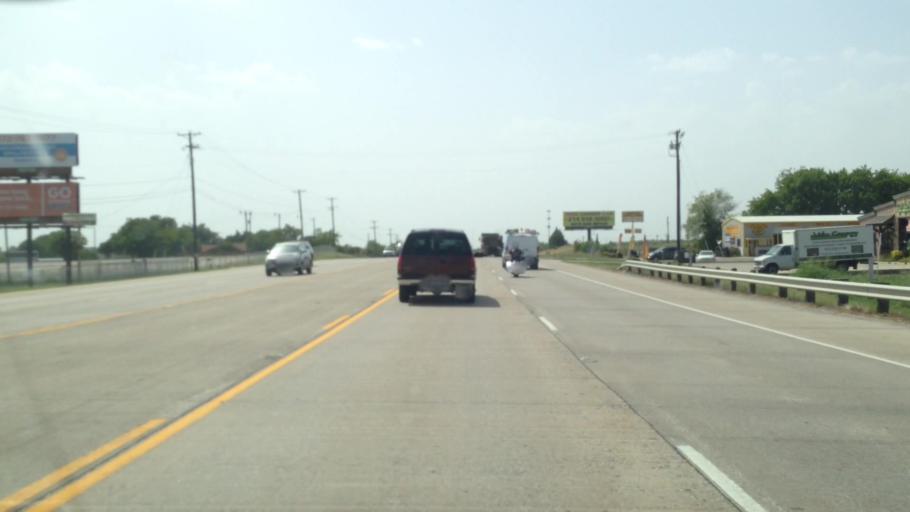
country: US
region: Texas
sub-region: Collin County
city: Lowry Crossing
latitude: 33.1866
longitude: -96.5410
